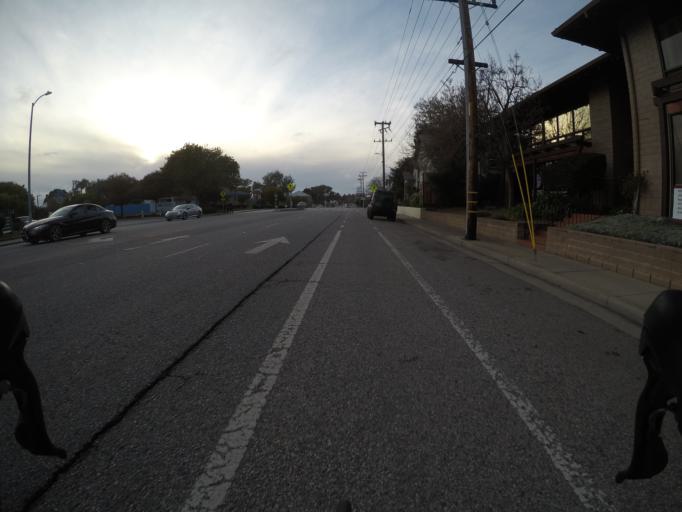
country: US
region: California
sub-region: Santa Cruz County
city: Capitola
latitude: 36.9738
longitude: -121.9622
